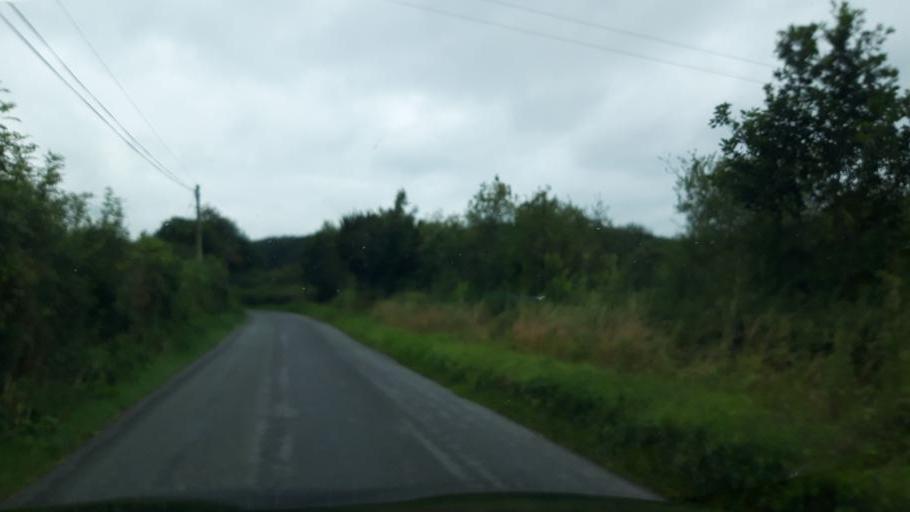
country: IE
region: Leinster
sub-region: Kilkenny
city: Ballyragget
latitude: 52.7211
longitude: -7.4032
